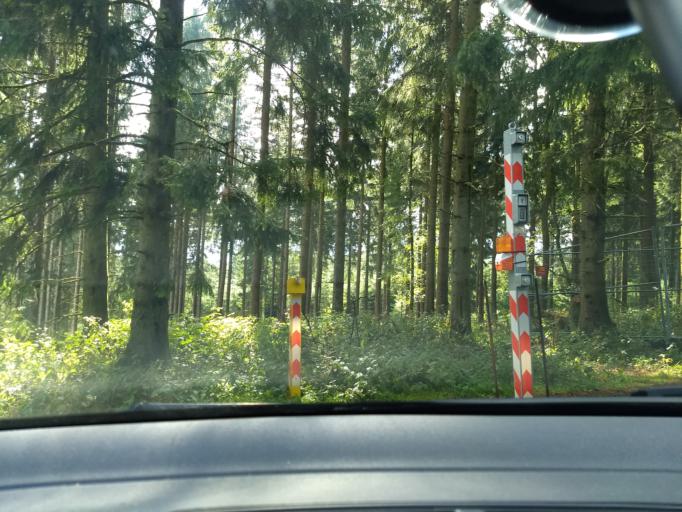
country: DE
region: North Rhine-Westphalia
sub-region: Regierungsbezirk Arnsberg
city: Finnentrop
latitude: 51.2134
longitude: 7.9991
